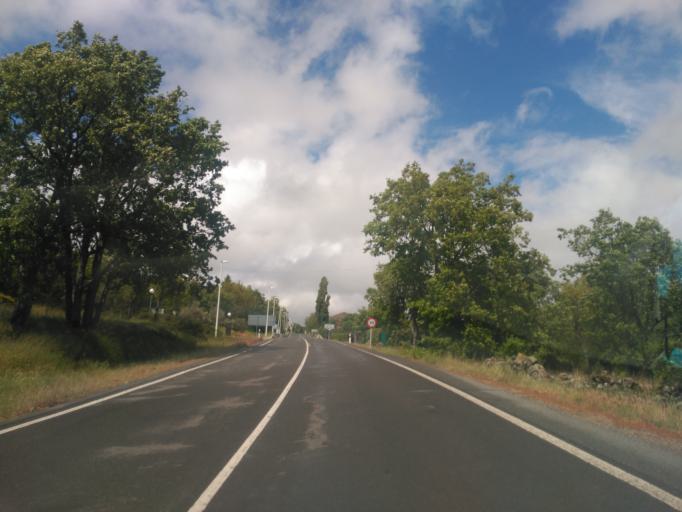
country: ES
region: Castille and Leon
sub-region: Provincia de Salamanca
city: Vallejera de Riofrio
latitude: 40.4053
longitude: -5.7236
